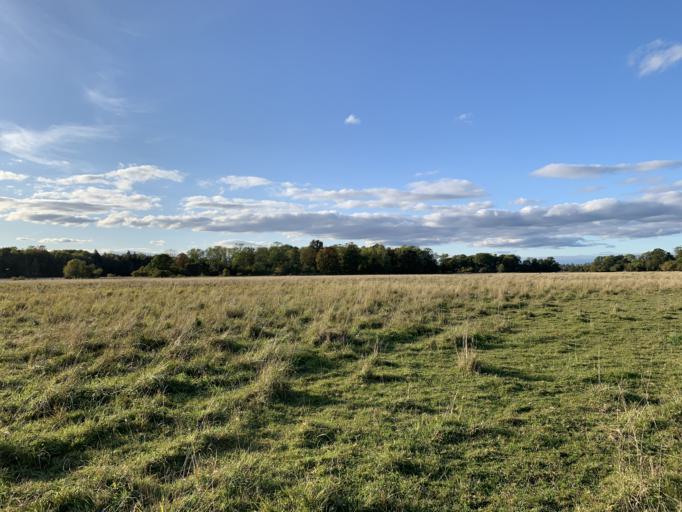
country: SE
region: Vaestmanland
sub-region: Hallstahammars Kommun
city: Kolback
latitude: 59.4779
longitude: 16.2222
